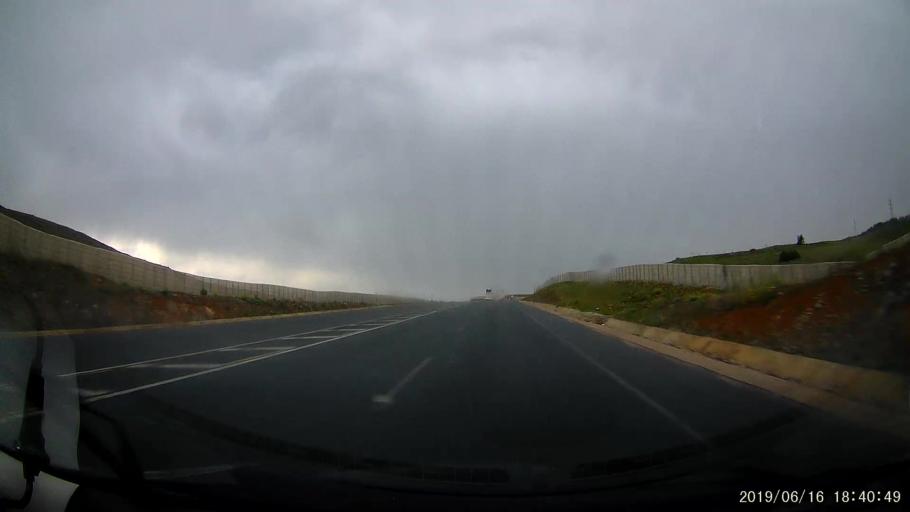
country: TR
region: Erzincan
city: Catalarmut
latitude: 39.8795
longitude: 39.1380
